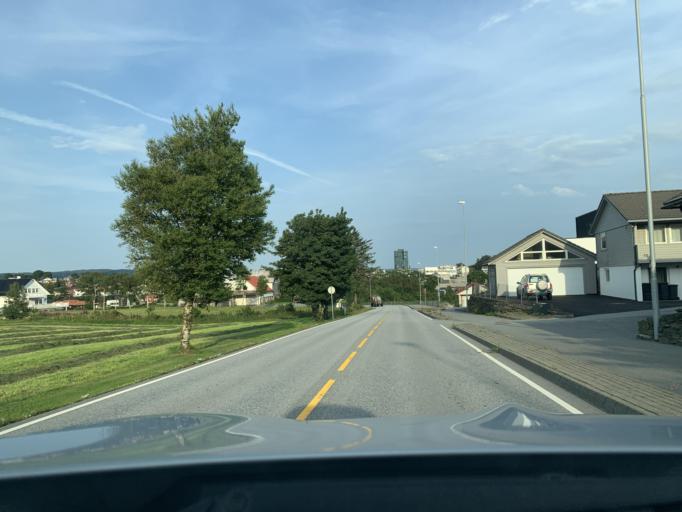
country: NO
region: Rogaland
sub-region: Time
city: Bryne
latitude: 58.7378
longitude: 5.6325
